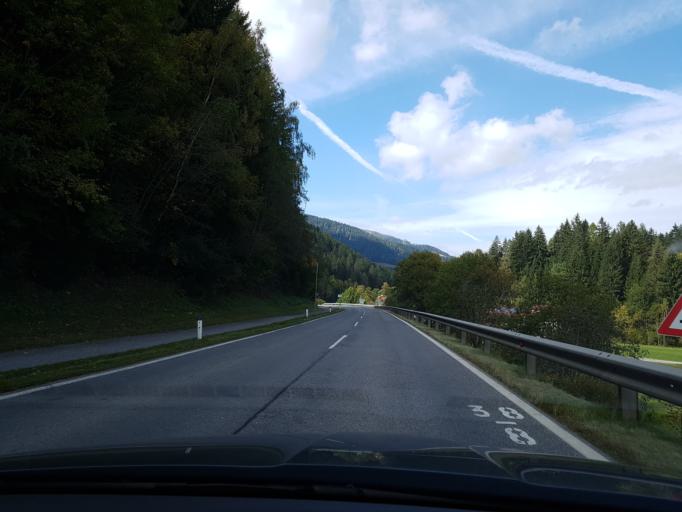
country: AT
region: Carinthia
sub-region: Politischer Bezirk Feldkirchen
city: Gnesau
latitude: 46.7781
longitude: 13.9517
